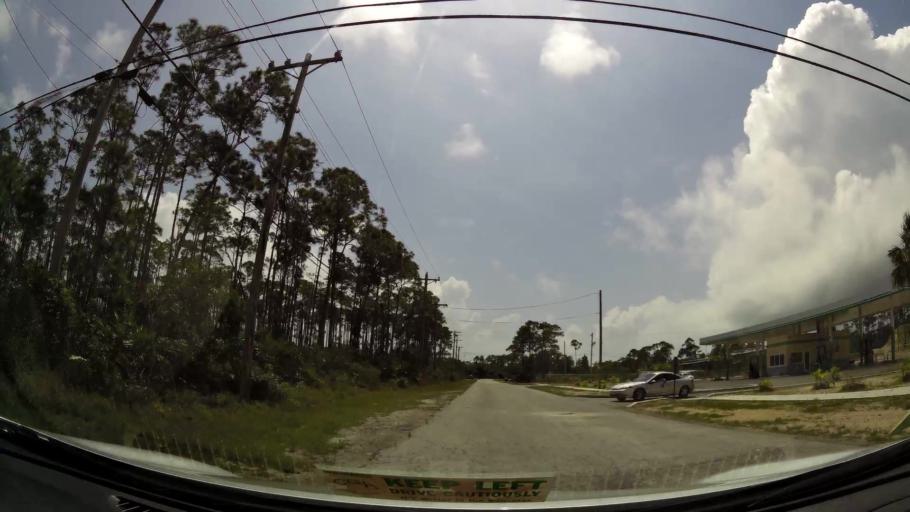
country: BS
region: Freeport
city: Lucaya
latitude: 26.5366
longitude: -78.6362
